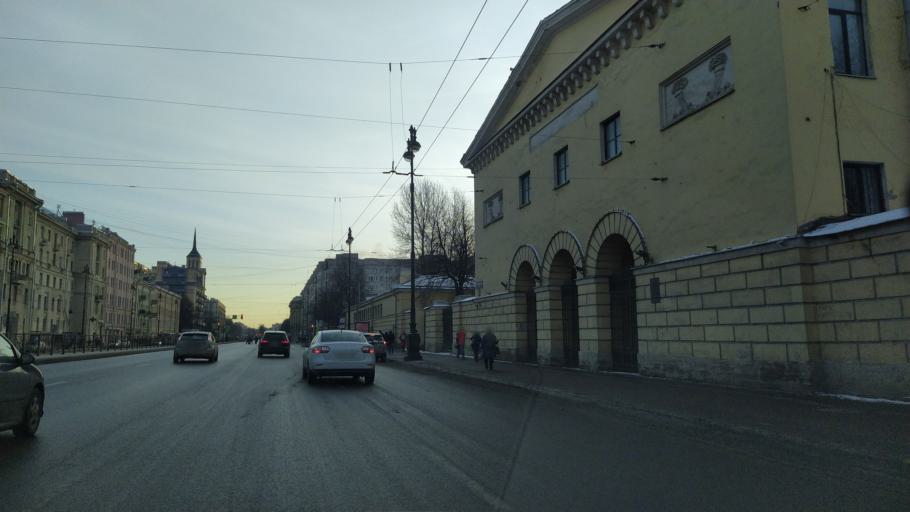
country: RU
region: St.-Petersburg
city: Saint Petersburg
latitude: 59.9076
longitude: 30.3182
